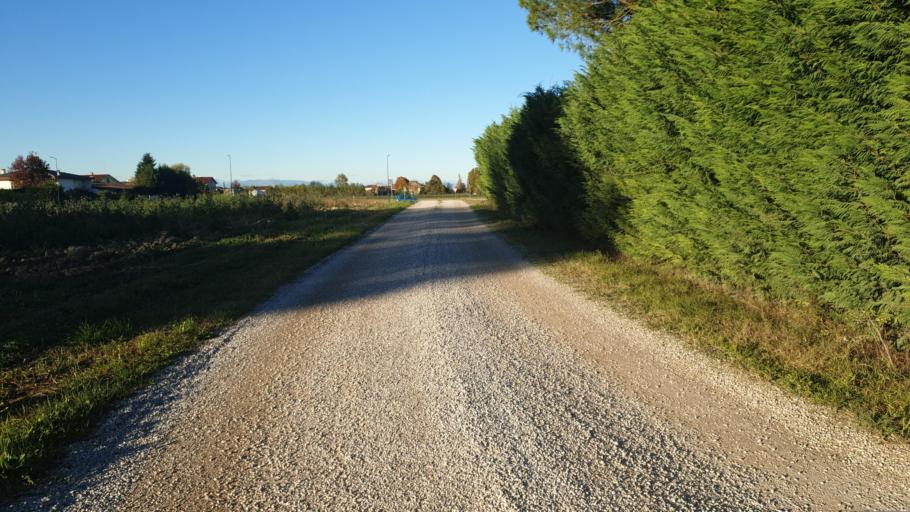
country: IT
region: Veneto
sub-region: Provincia di Venezia
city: Scaltenigo
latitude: 45.4688
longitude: 12.0863
